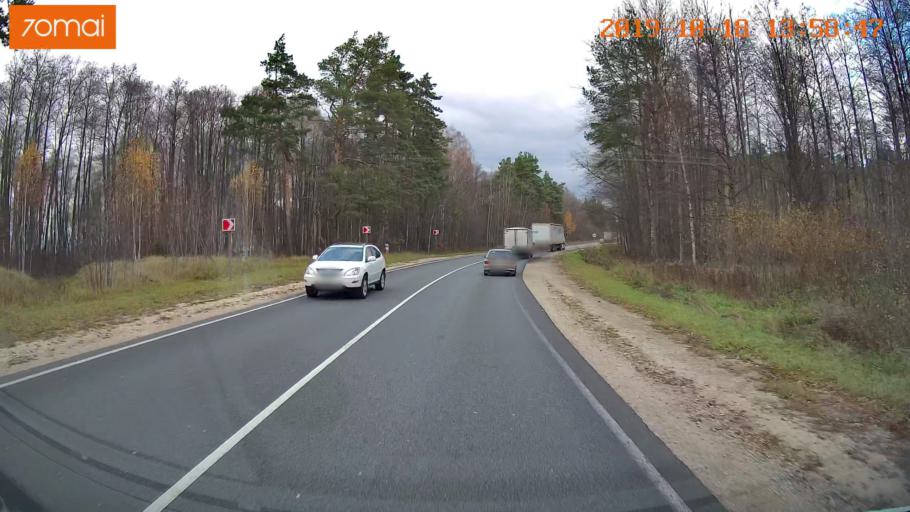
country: RU
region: Rjazan
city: Spas-Klepiki
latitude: 55.0883
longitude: 40.0570
